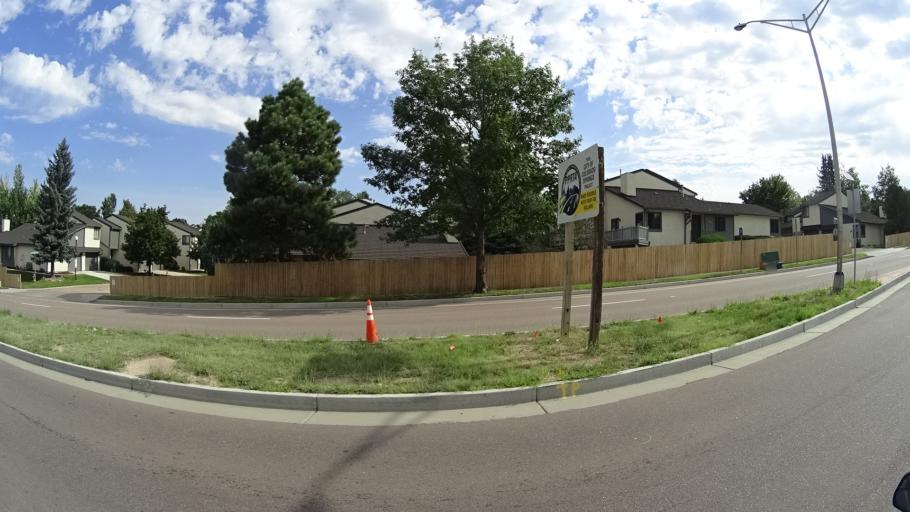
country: US
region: Colorado
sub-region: El Paso County
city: Cimarron Hills
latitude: 38.8965
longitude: -104.7348
